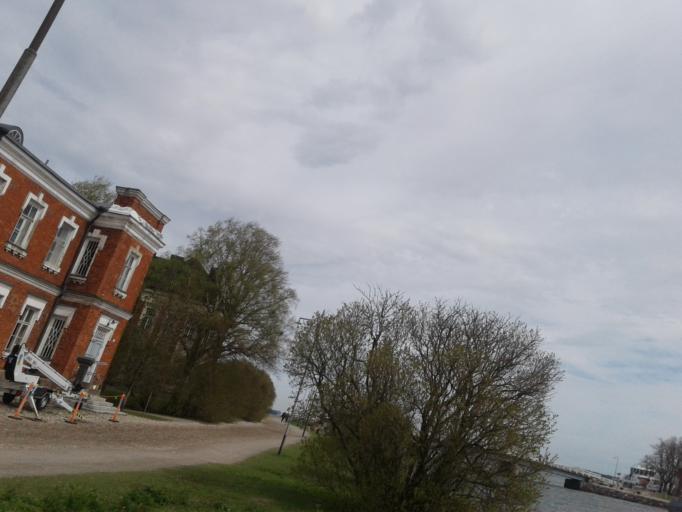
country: FI
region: Uusimaa
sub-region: Helsinki
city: Helsinki
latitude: 60.1482
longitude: 24.9799
